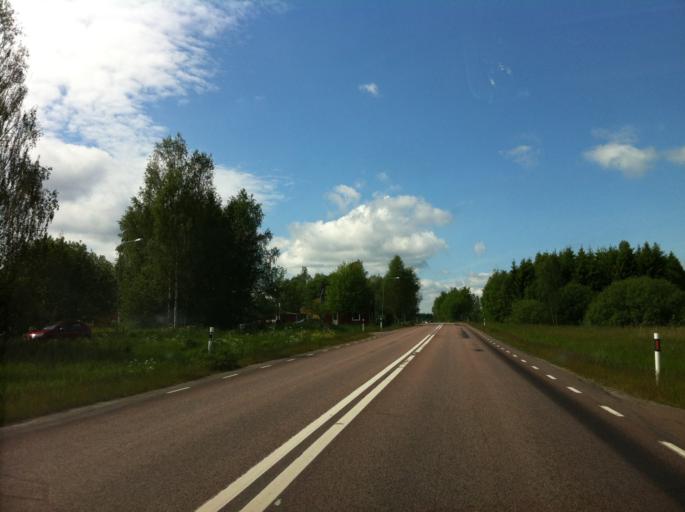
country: SE
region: Vaermland
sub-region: Karlstads Kommun
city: Valberg
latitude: 59.3778
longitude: 13.1587
